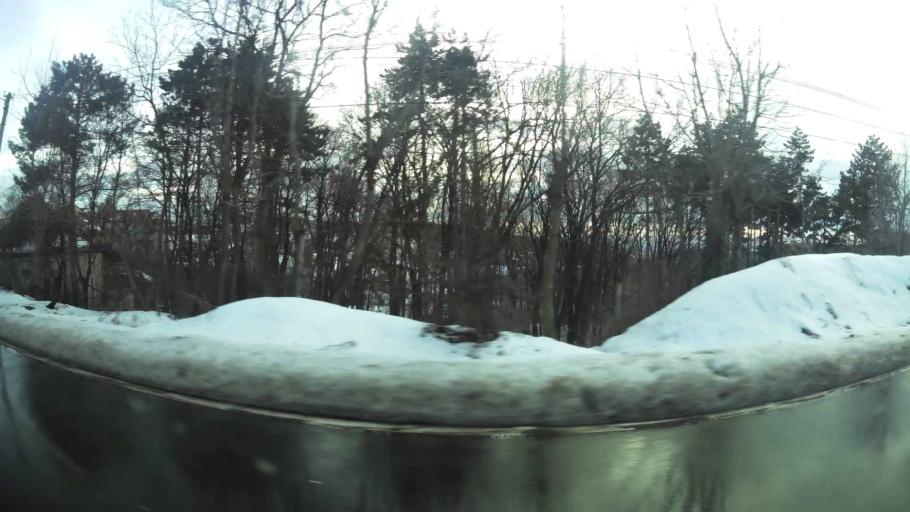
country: RS
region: Central Serbia
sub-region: Belgrade
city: Zvezdara
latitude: 44.7390
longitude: 20.5120
